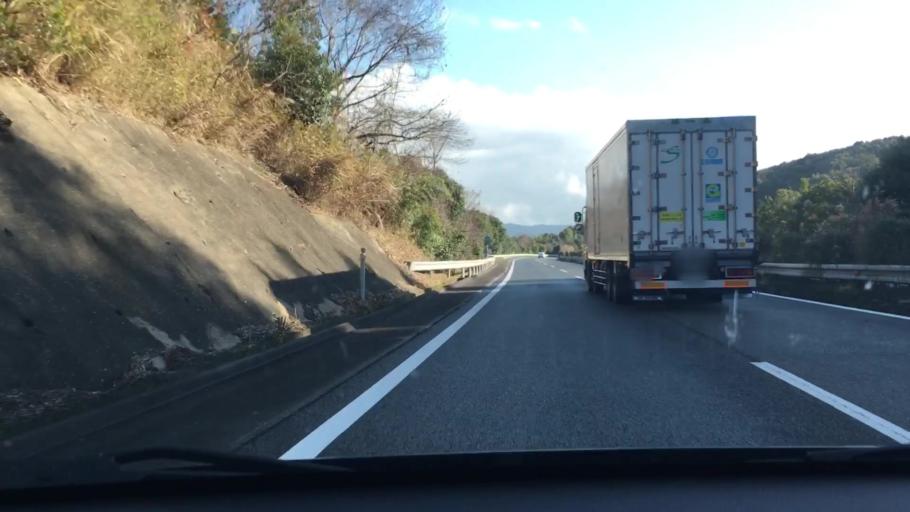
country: JP
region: Kumamoto
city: Hitoyoshi
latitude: 32.1712
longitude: 130.7912
